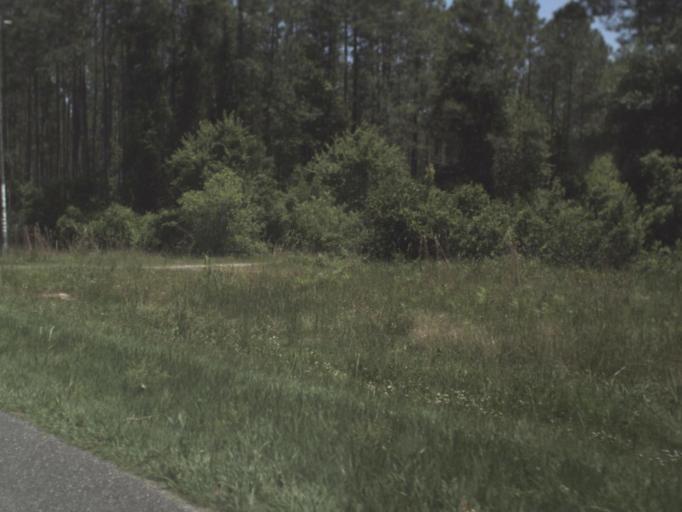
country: US
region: Florida
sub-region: Columbia County
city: Watertown
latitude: 30.1884
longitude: -82.5470
